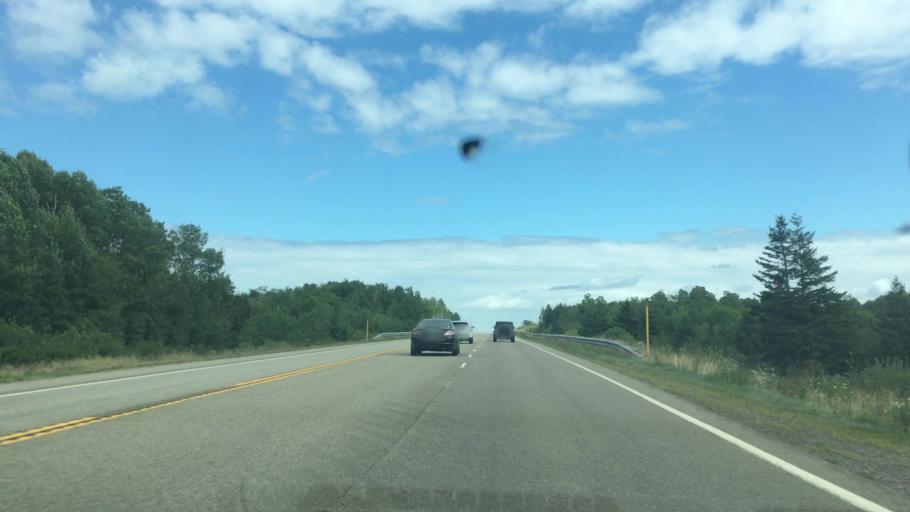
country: CA
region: Nova Scotia
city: Port Hawkesbury
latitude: 45.6215
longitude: -61.6093
